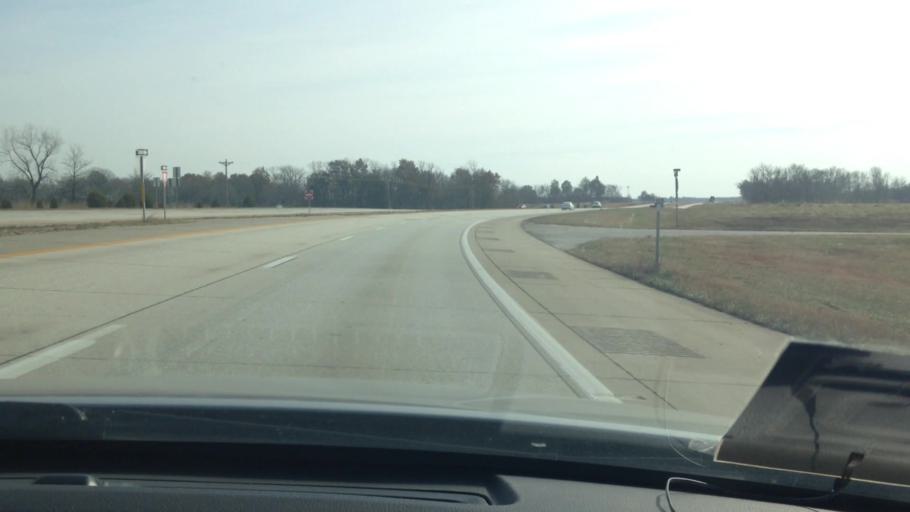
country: US
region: Missouri
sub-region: Henry County
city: Clinton
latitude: 38.4627
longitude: -93.9707
